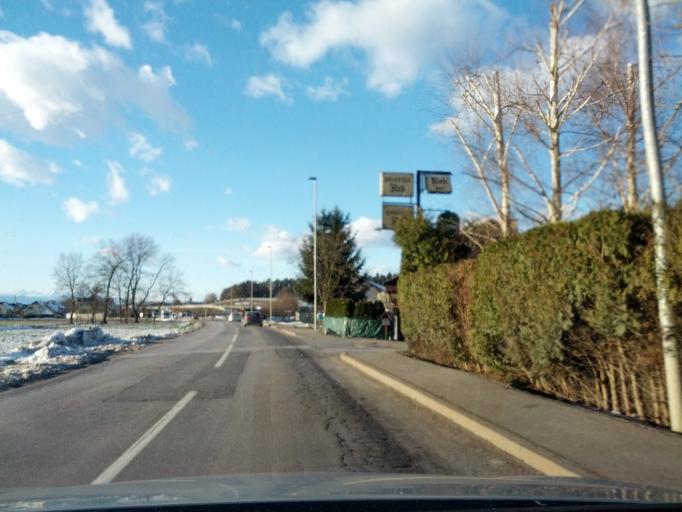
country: SI
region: Domzale
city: Dob
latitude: 46.1502
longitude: 14.6578
